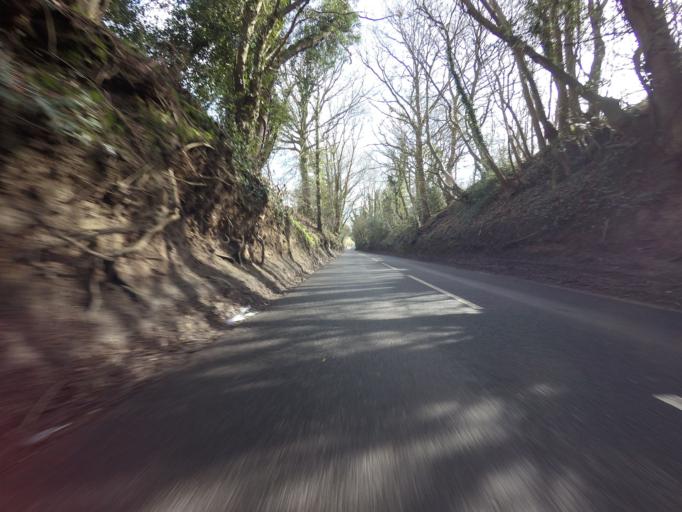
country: GB
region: England
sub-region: Greater London
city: Orpington
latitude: 51.3860
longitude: 0.1350
